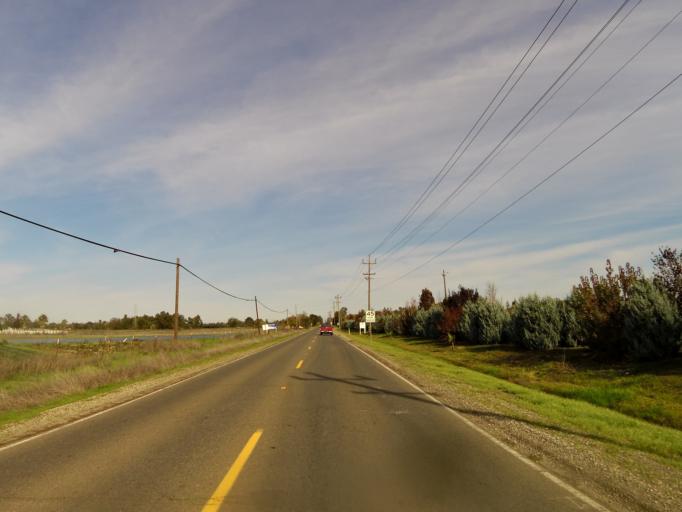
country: US
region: California
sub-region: Sacramento County
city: Wilton
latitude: 38.4169
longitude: -121.3164
